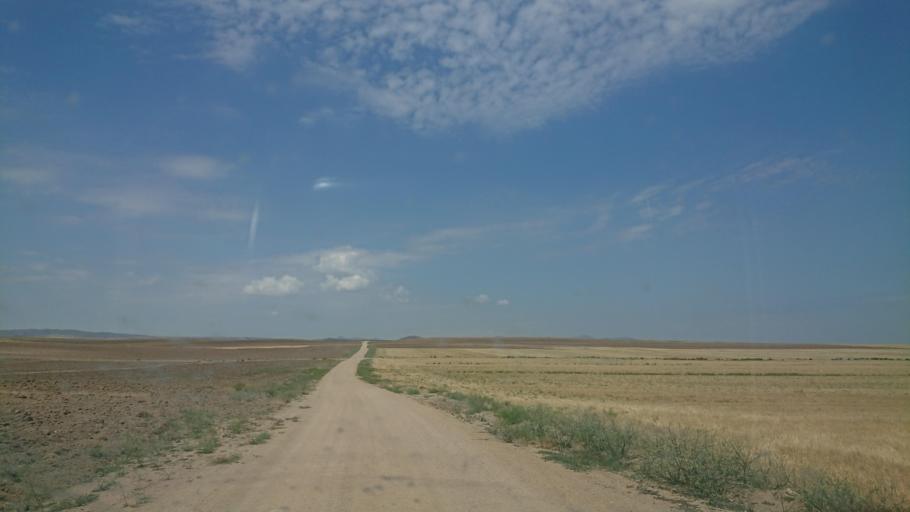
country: TR
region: Aksaray
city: Agacoren
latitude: 38.9548
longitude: 33.9353
